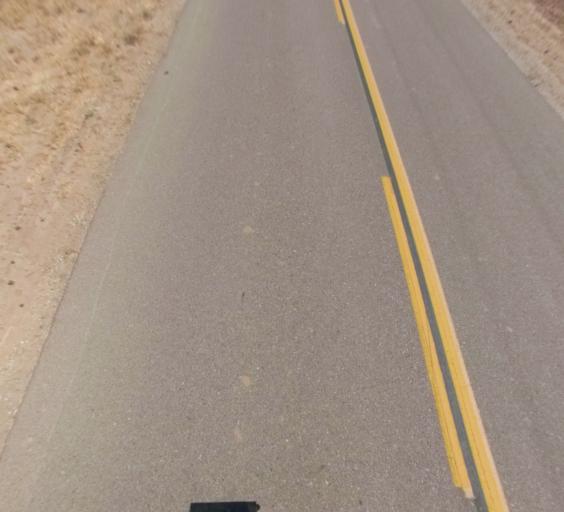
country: US
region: California
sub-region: Madera County
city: Bonadelle Ranchos-Madera Ranchos
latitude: 37.0008
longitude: -119.8649
